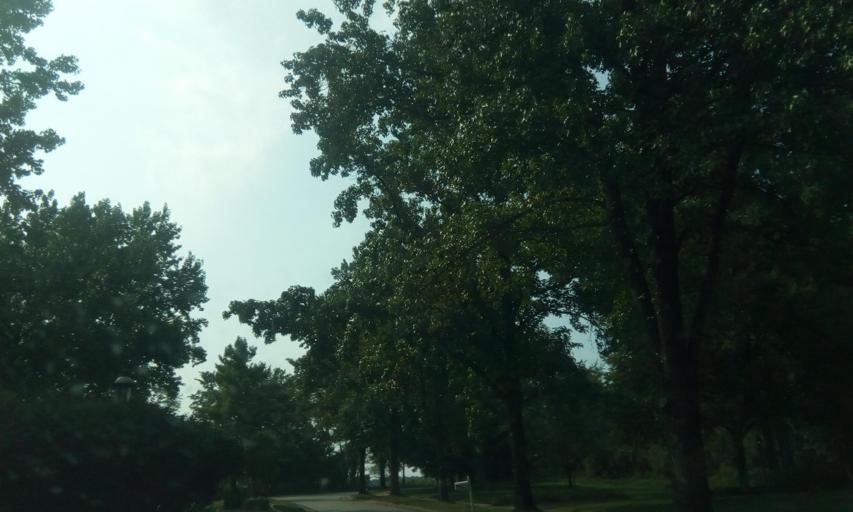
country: US
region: Missouri
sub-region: Saint Louis County
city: Town and Country
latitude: 38.6121
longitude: -90.4839
